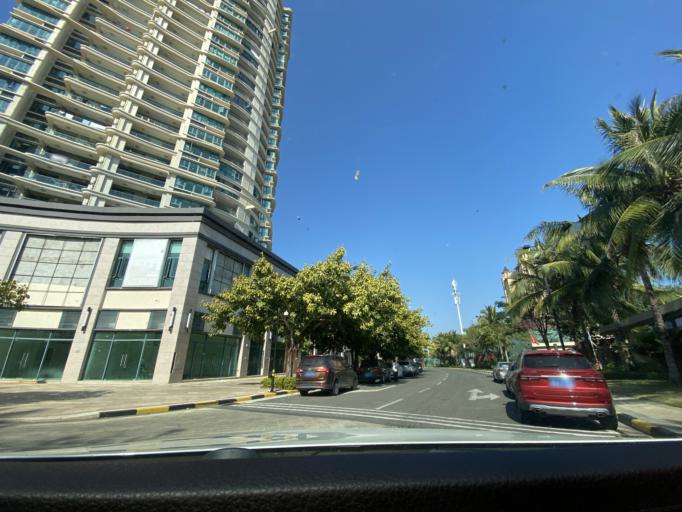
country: CN
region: Hainan
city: Yingzhou
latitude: 18.4080
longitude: 109.8760
